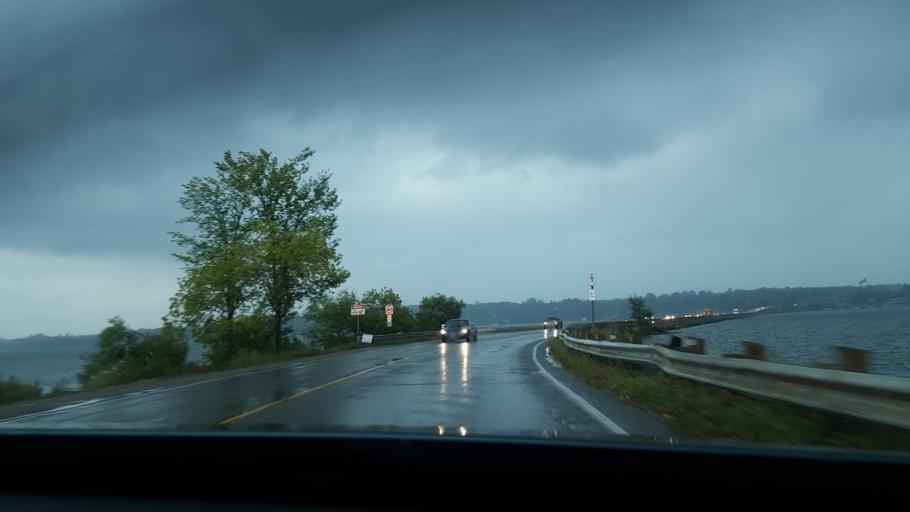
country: CA
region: Ontario
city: Peterborough
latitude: 44.3879
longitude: -78.3982
